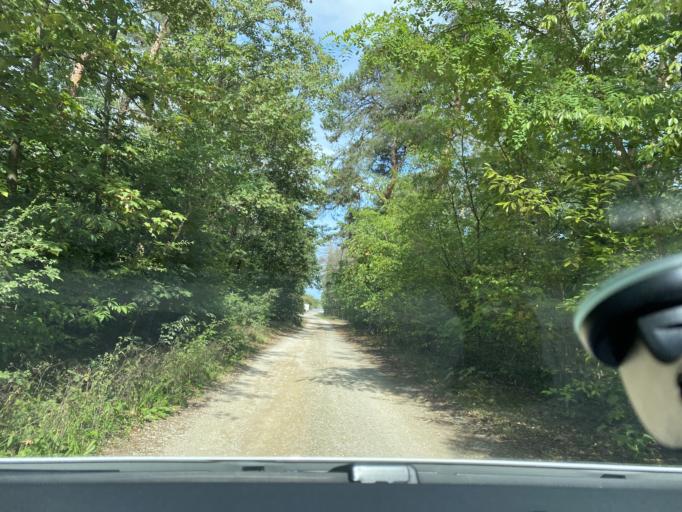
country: DE
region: Bavaria
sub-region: Regierungsbezirk Mittelfranken
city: Furth
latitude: 49.5004
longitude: 10.9921
